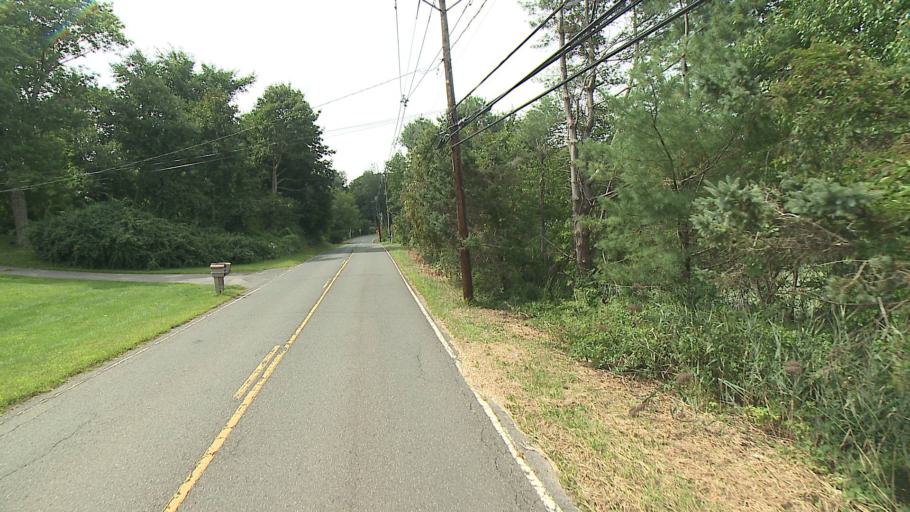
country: US
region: Connecticut
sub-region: Litchfield County
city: Bethlehem Village
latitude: 41.6395
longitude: -73.2115
